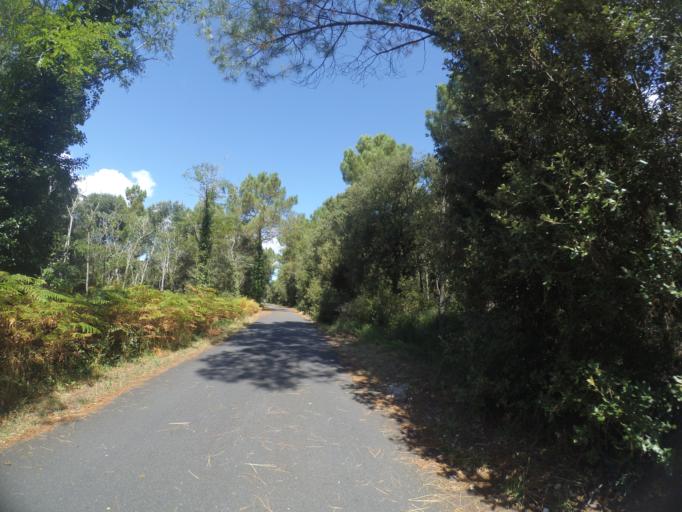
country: FR
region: Poitou-Charentes
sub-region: Departement de la Charente-Maritime
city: Les Mathes
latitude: 45.6768
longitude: -1.1526
